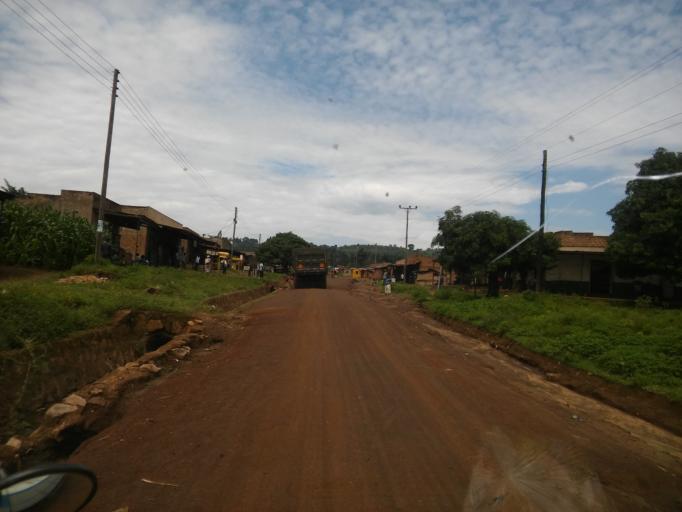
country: UG
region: Eastern Region
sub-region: Tororo District
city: Tororo
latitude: 0.8235
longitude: 34.2929
